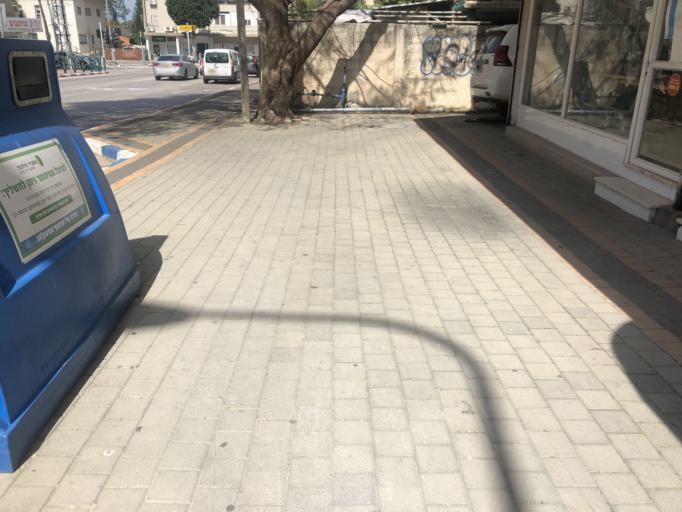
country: IL
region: Haifa
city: Hadera
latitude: 32.4396
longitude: 34.9180
